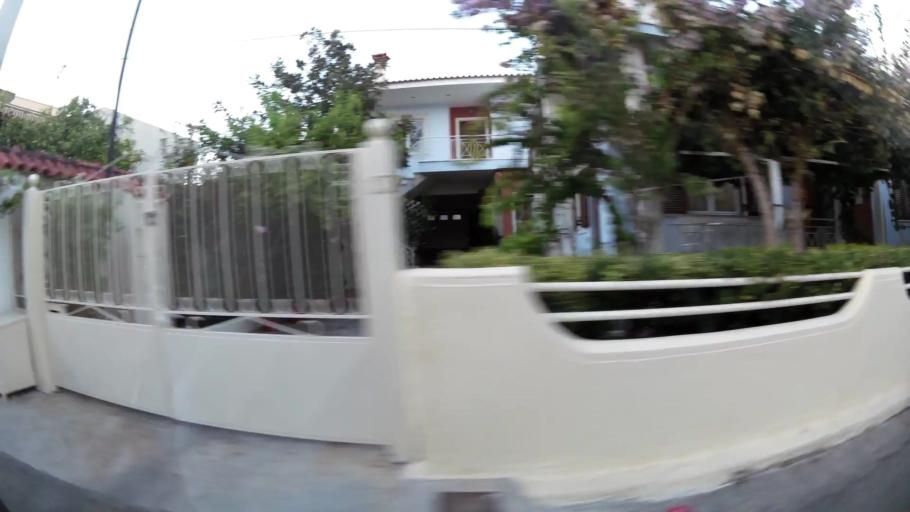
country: GR
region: Attica
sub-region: Nomarchia Anatolikis Attikis
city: Spata
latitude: 37.9626
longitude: 23.9162
